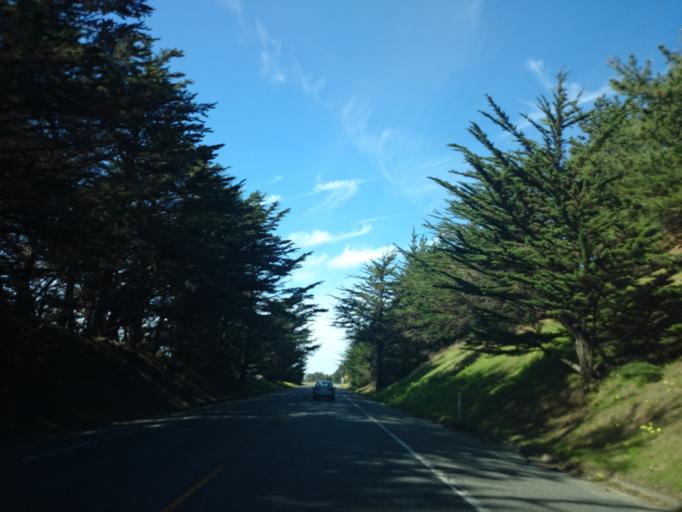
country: US
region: California
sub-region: San Mateo County
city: Moss Beach
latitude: 37.5192
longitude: -122.5034
